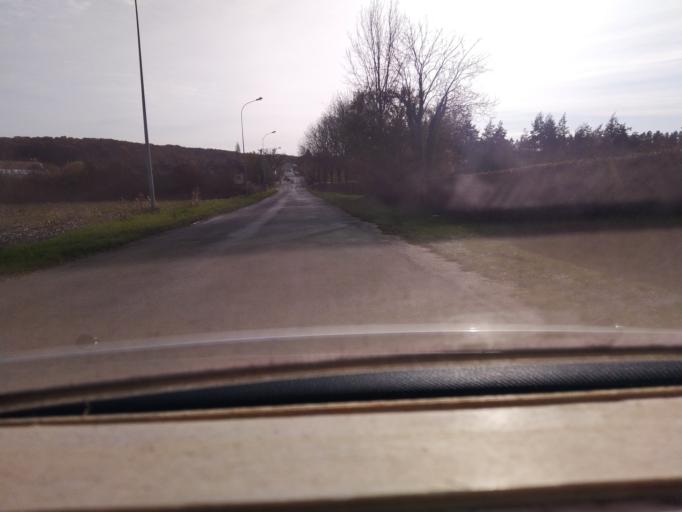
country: FR
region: Haute-Normandie
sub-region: Departement de la Seine-Maritime
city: Yainville
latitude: 49.4578
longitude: 0.8265
